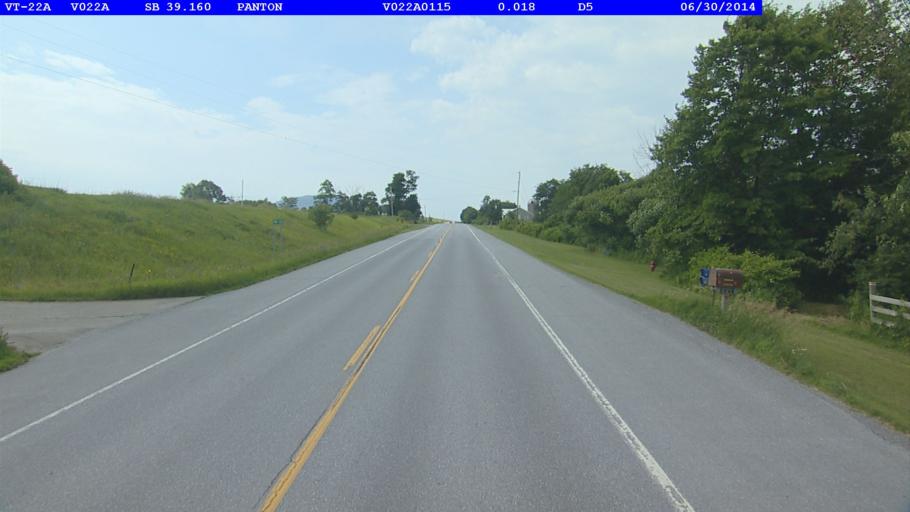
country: US
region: Vermont
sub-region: Addison County
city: Vergennes
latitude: 44.1199
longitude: -73.2936
